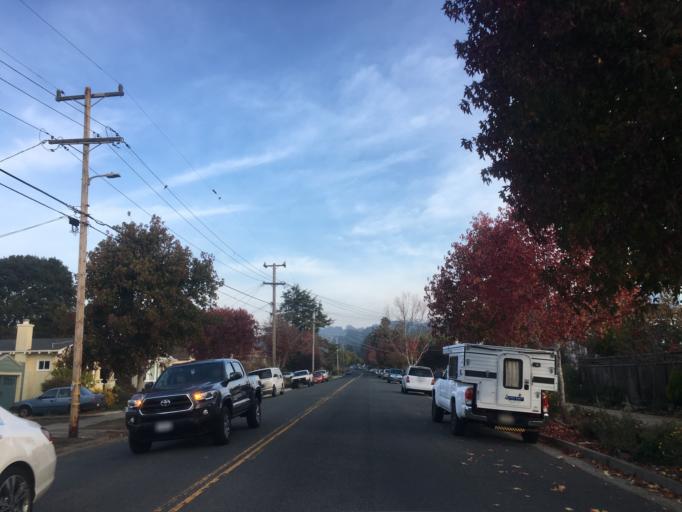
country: US
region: California
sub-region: Alameda County
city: Albany
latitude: 37.8966
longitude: -122.2881
